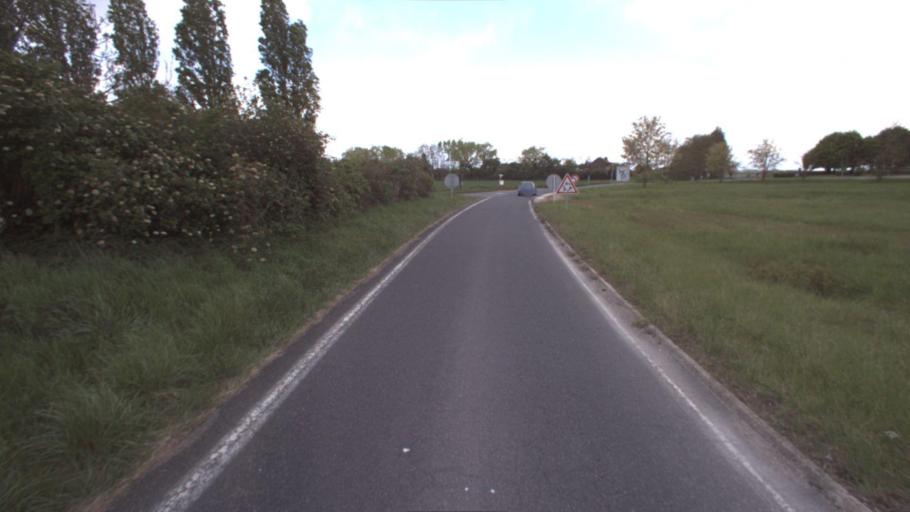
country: FR
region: Ile-de-France
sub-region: Departement de Seine-et-Marne
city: Rozay-en-Brie
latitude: 48.6876
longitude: 2.9660
